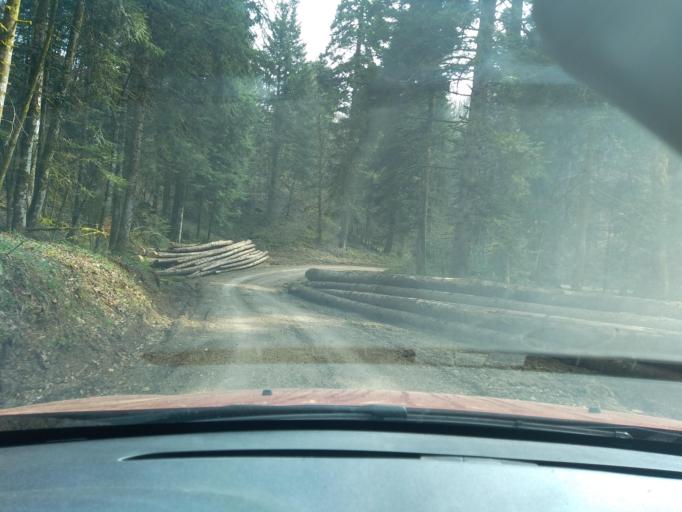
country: FR
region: Franche-Comte
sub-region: Departement du Jura
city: Moirans-en-Montagne
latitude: 46.4742
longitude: 5.7589
